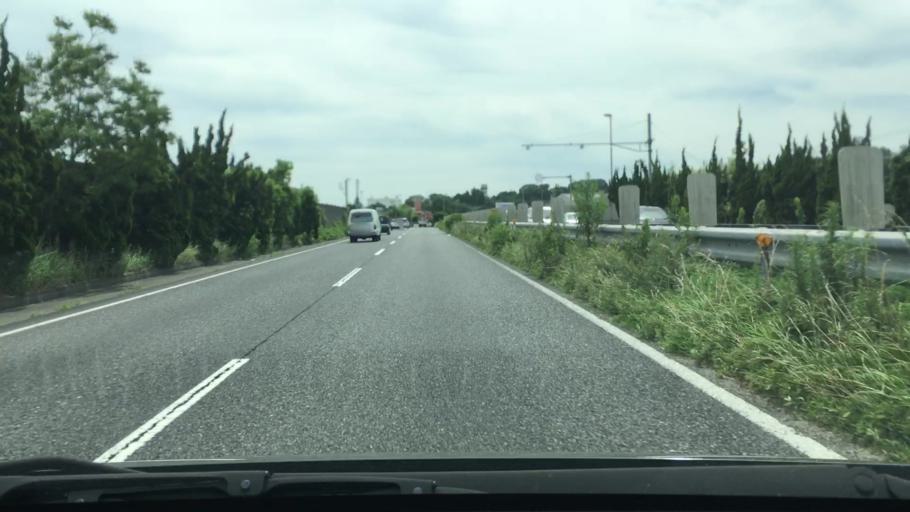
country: JP
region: Hiroshima
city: Hatsukaichi
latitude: 34.3774
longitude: 132.3461
